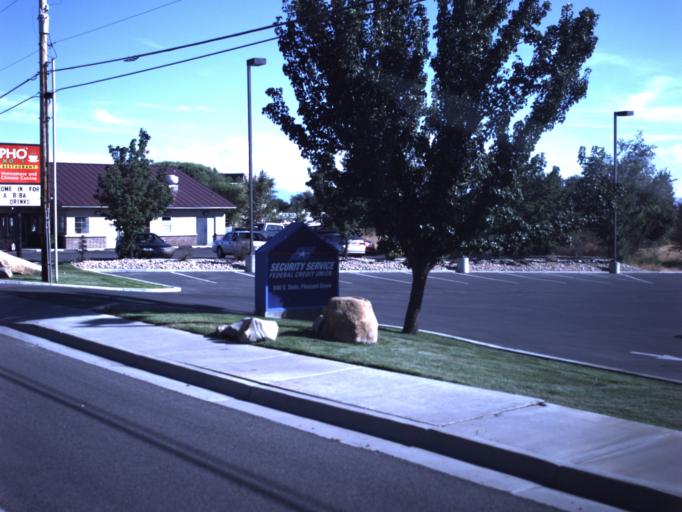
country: US
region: Utah
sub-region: Utah County
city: Pleasant Grove
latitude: 40.3539
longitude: -111.7342
